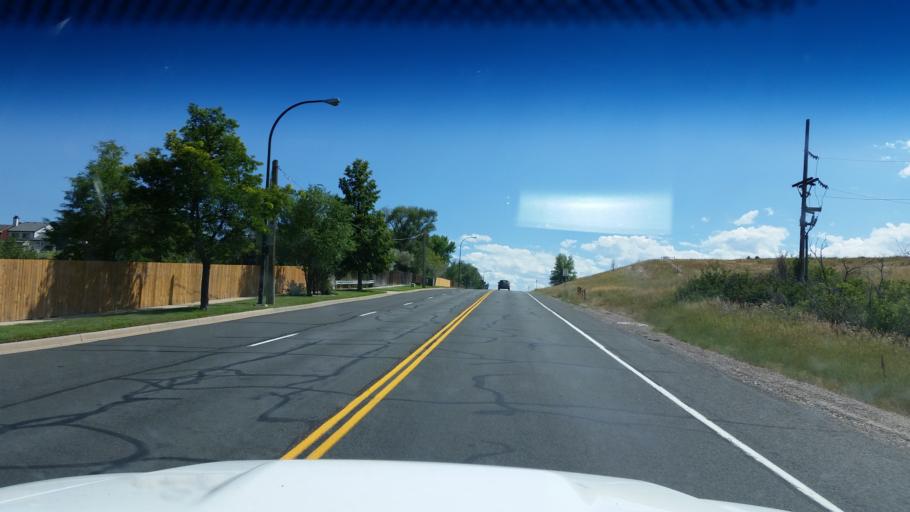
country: US
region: Colorado
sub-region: Broomfield County
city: Broomfield
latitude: 39.8860
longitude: -105.1289
